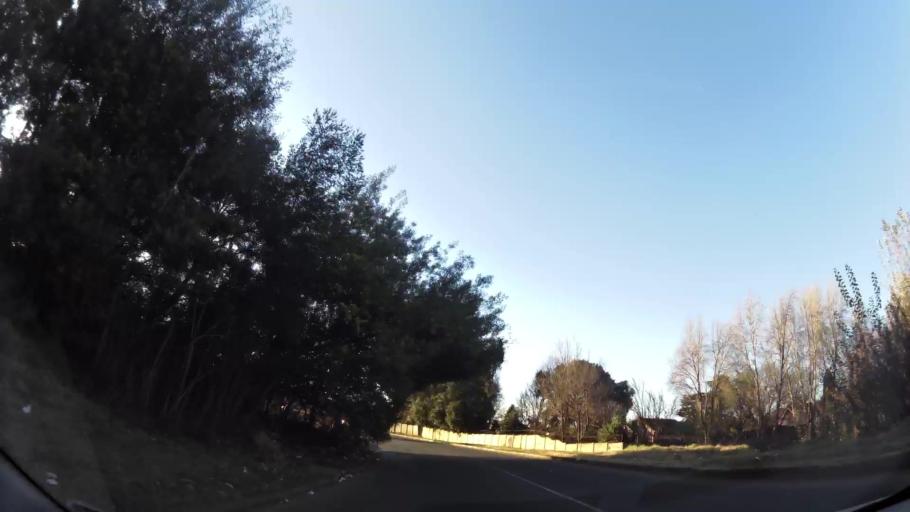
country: ZA
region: Gauteng
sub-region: City of Johannesburg Metropolitan Municipality
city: Roodepoort
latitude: -26.1774
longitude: 27.9355
